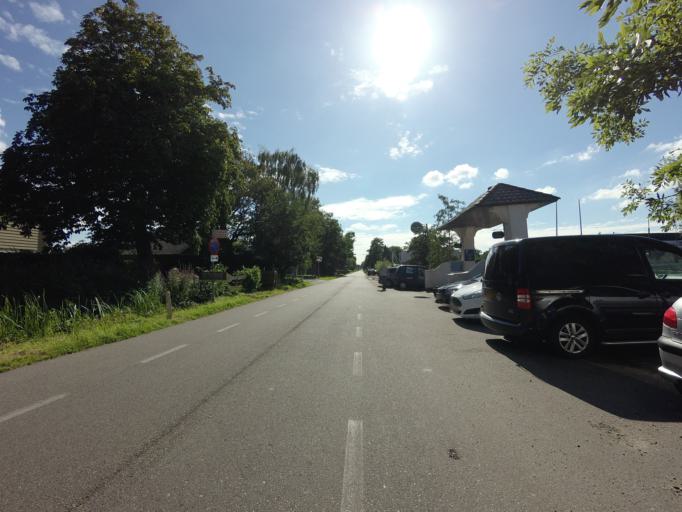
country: NL
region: Utrecht
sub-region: Stichtse Vecht
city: Vreeland
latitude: 52.2375
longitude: 4.9700
